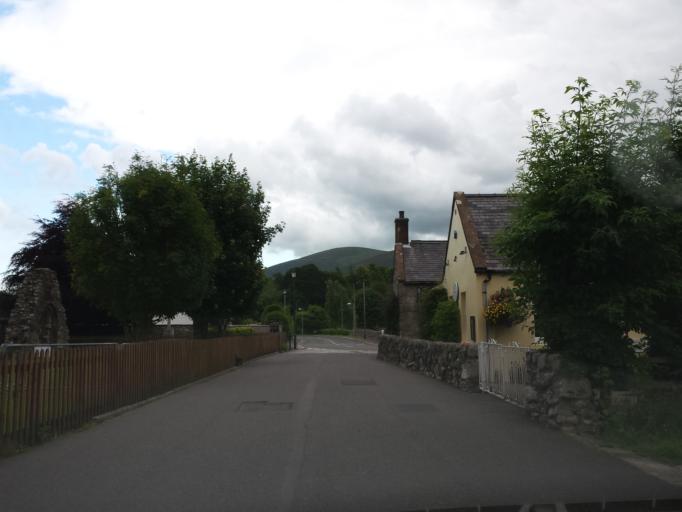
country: GB
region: Scotland
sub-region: Dumfries and Galloway
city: Dumfries
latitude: 54.9803
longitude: -3.6195
